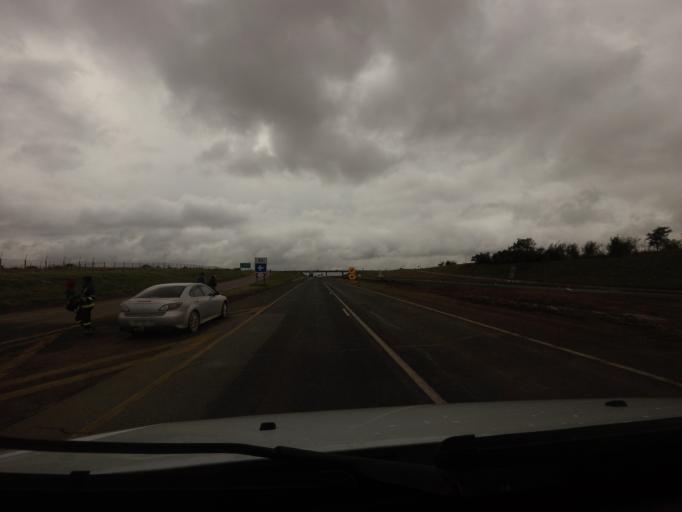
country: ZA
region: Mpumalanga
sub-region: Nkangala District Municipality
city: Witbank
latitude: -25.8738
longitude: 29.1316
